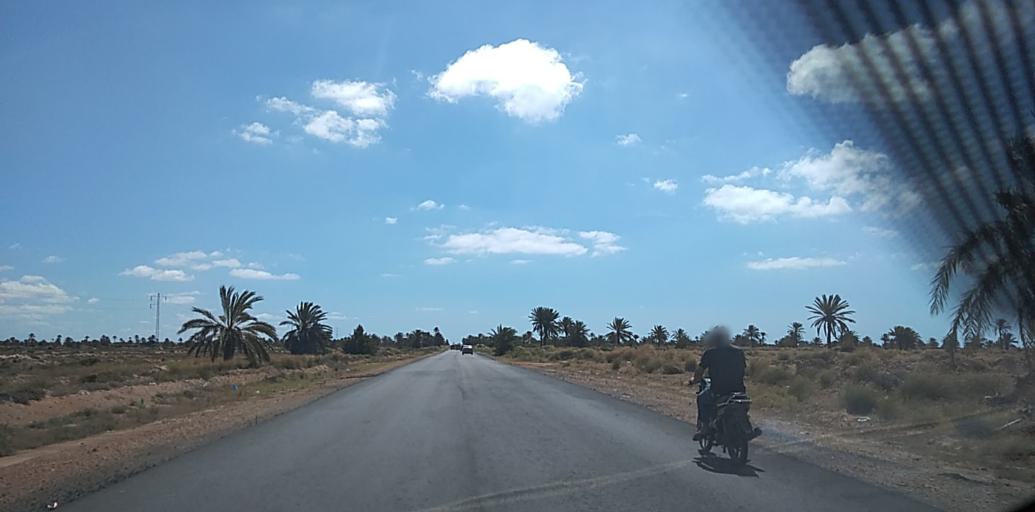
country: TN
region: Safaqis
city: Al Qarmadah
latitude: 34.6590
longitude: 11.1067
